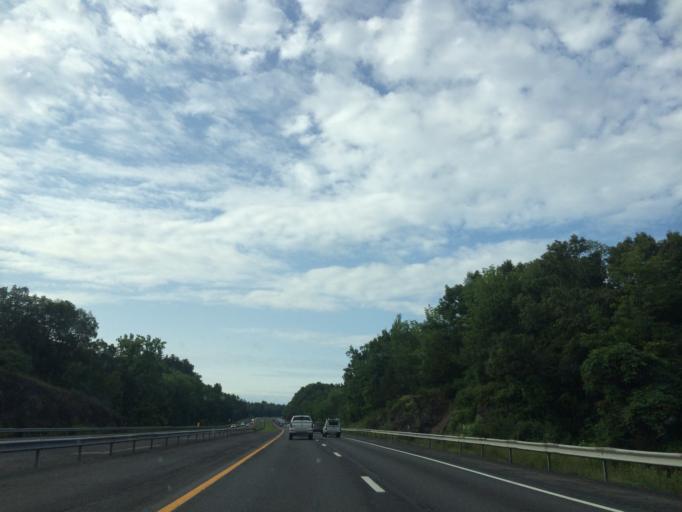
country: US
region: New York
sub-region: Ulster County
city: Tillson
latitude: 41.8165
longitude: -74.0561
